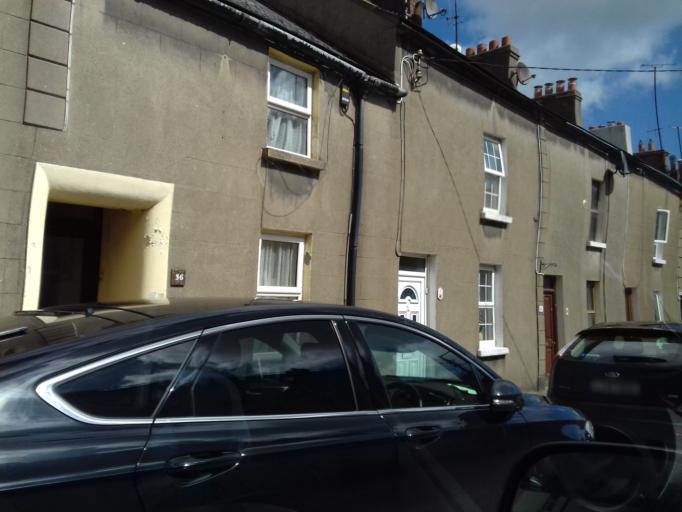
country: IE
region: Leinster
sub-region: Loch Garman
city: Loch Garman
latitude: 52.3343
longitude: -6.4565
